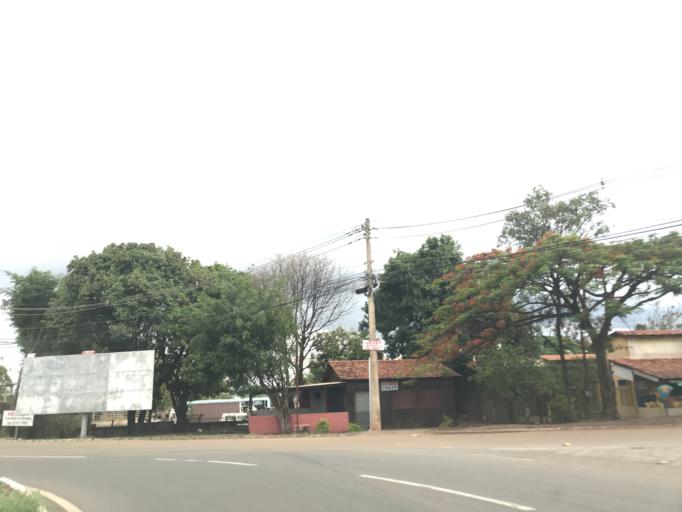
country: BR
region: Federal District
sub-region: Brasilia
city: Brasilia
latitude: -15.8011
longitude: -47.9716
